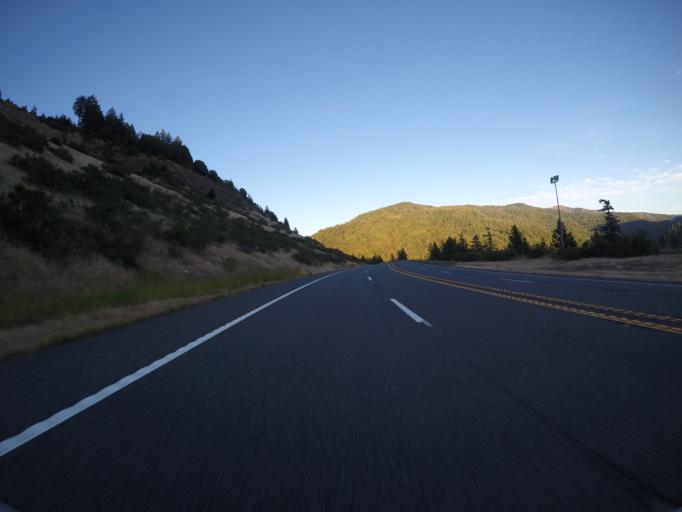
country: US
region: California
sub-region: Mendocino County
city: Laytonville
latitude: 39.8292
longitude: -123.6590
